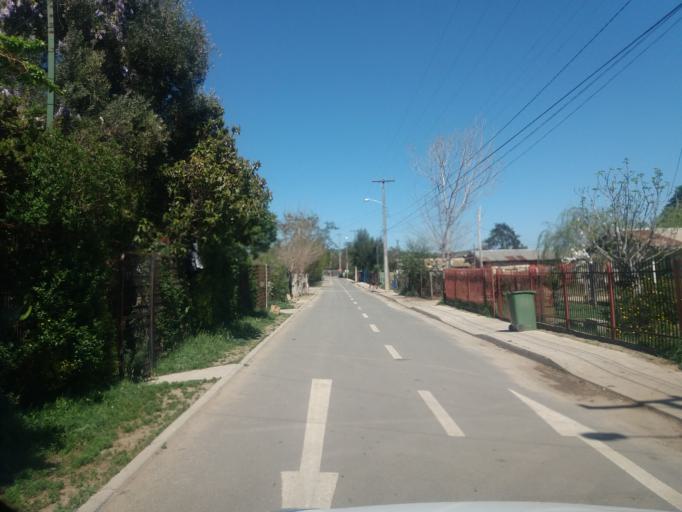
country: CL
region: Valparaiso
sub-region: Provincia de Marga Marga
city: Limache
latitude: -32.9820
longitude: -71.2906
